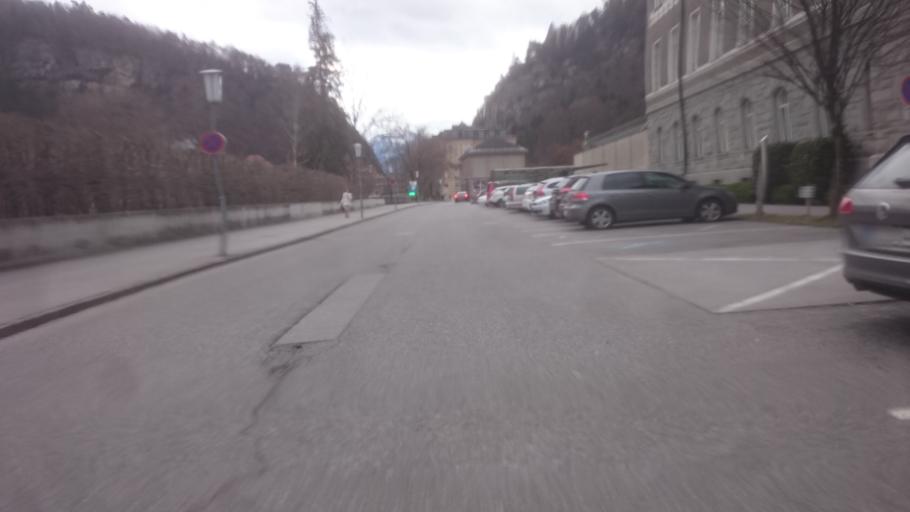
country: AT
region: Vorarlberg
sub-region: Politischer Bezirk Feldkirch
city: Feldkirch
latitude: 47.2368
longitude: 9.5931
